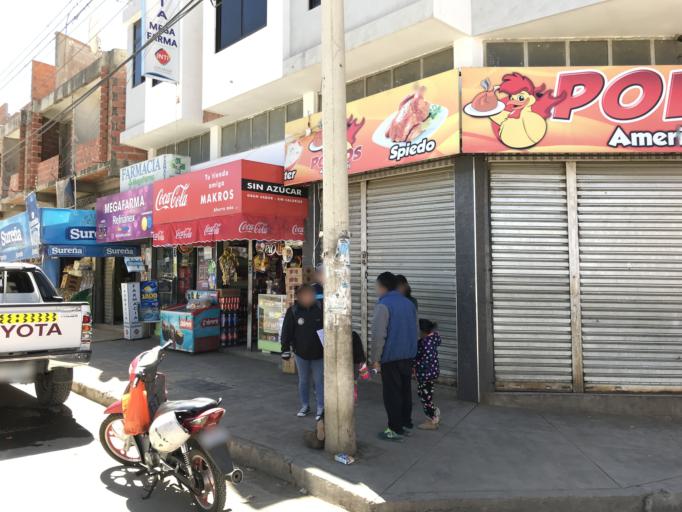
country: BO
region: Chuquisaca
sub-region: Provincia Oropeza
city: Huata
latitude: -19.0212
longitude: -65.2484
